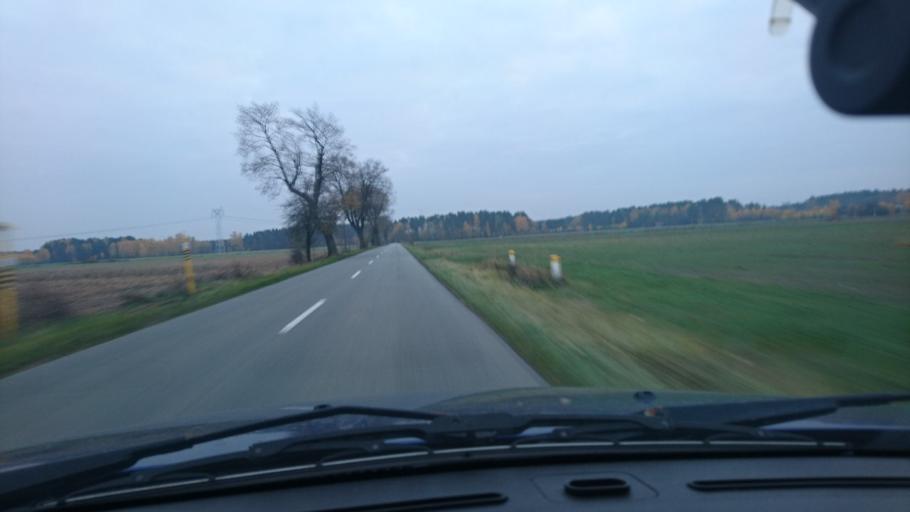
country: PL
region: Greater Poland Voivodeship
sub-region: Powiat ostrowski
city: Odolanow
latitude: 51.5362
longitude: 17.6506
